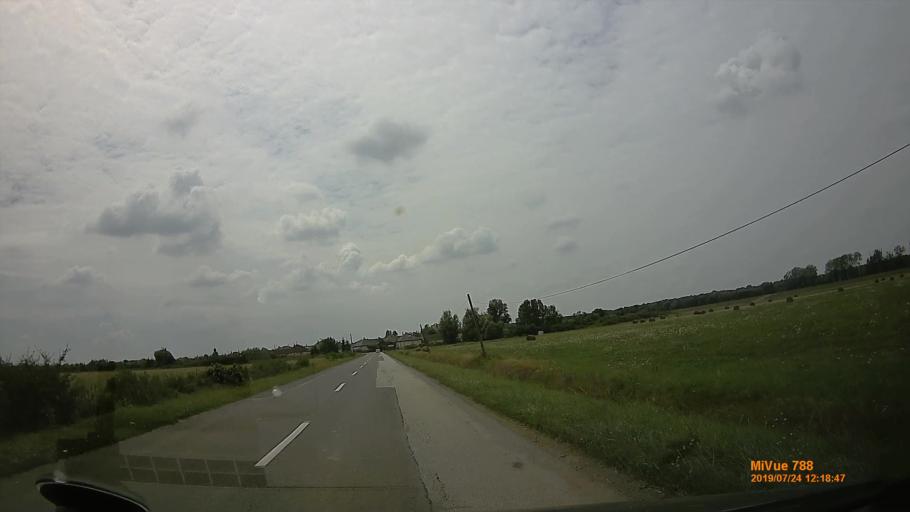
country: HU
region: Szabolcs-Szatmar-Bereg
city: Vasarosnameny
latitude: 48.1468
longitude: 22.3466
